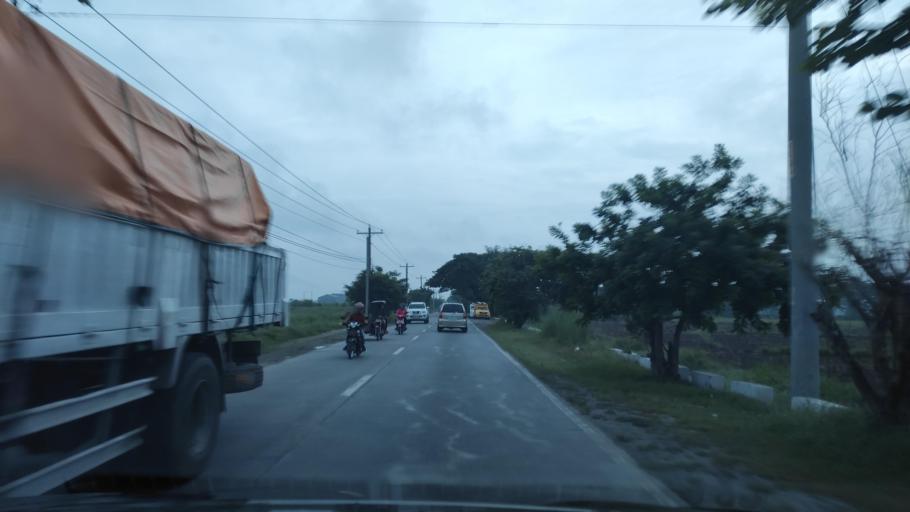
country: PH
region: Central Luzon
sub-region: Province of Pampanga
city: Laug
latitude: 15.0532
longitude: 120.7527
